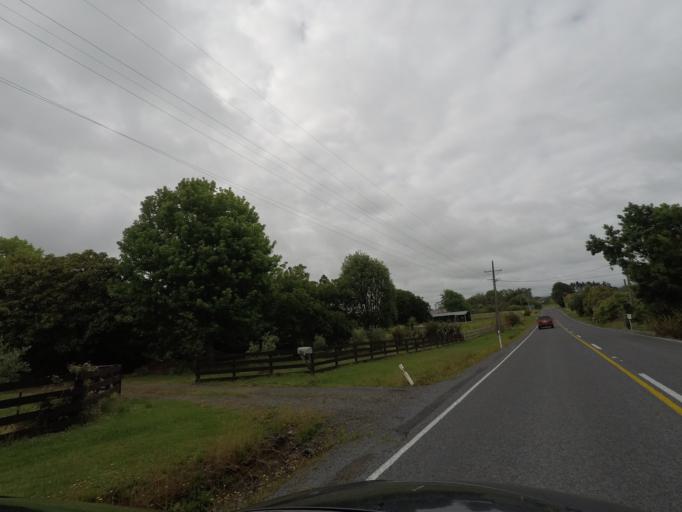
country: NZ
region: Auckland
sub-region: Auckland
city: Rosebank
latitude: -36.7968
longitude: 174.5740
